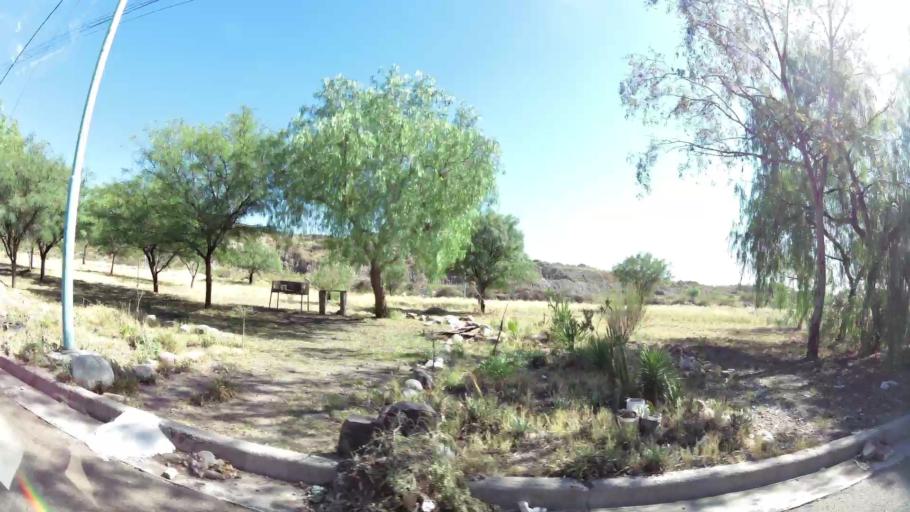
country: AR
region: Mendoza
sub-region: Departamento de Godoy Cruz
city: Godoy Cruz
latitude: -32.9001
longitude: -68.8884
